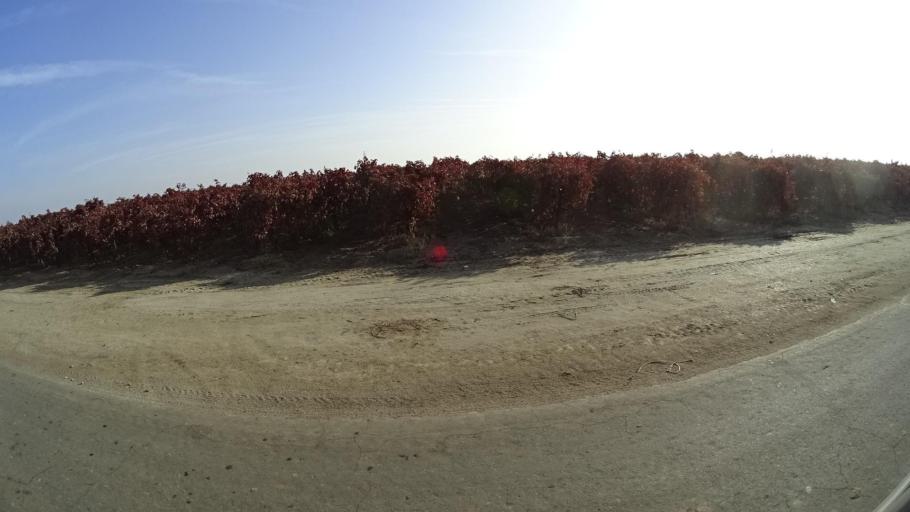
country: US
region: California
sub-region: Kern County
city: McFarland
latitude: 35.6866
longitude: -119.1870
